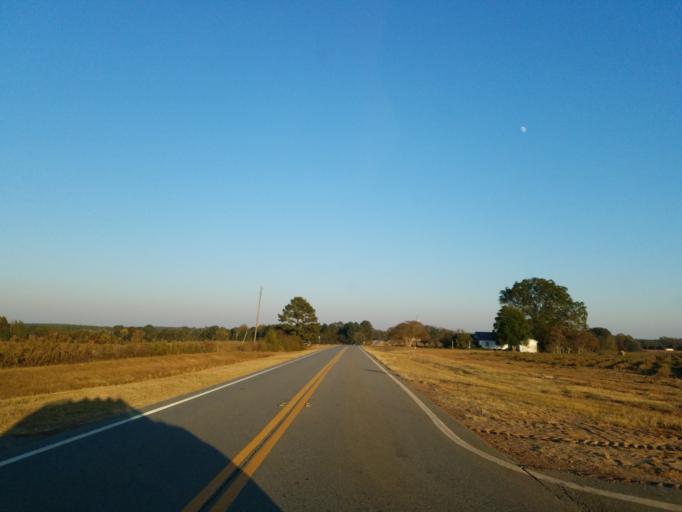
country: US
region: Georgia
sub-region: Wilcox County
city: Rochelle
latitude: 31.8159
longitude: -83.5192
